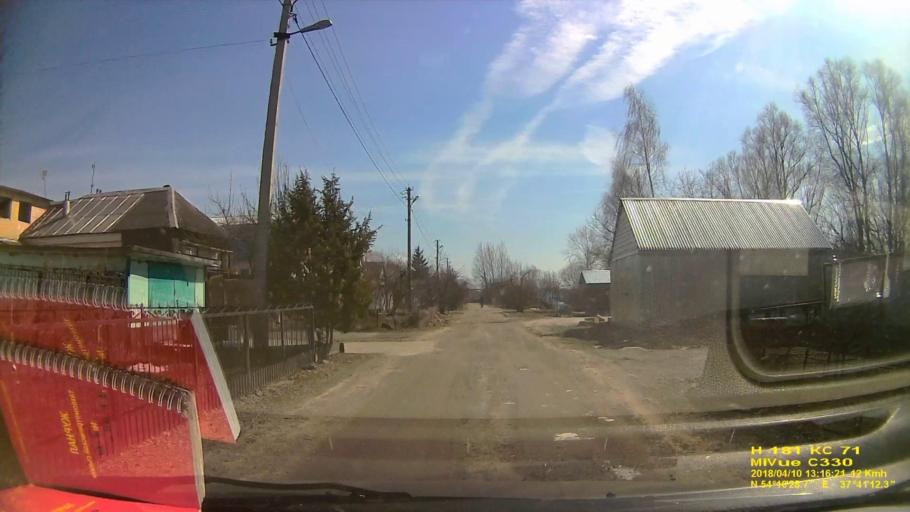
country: RU
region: Tula
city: Tula
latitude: 54.1746
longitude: 37.6868
